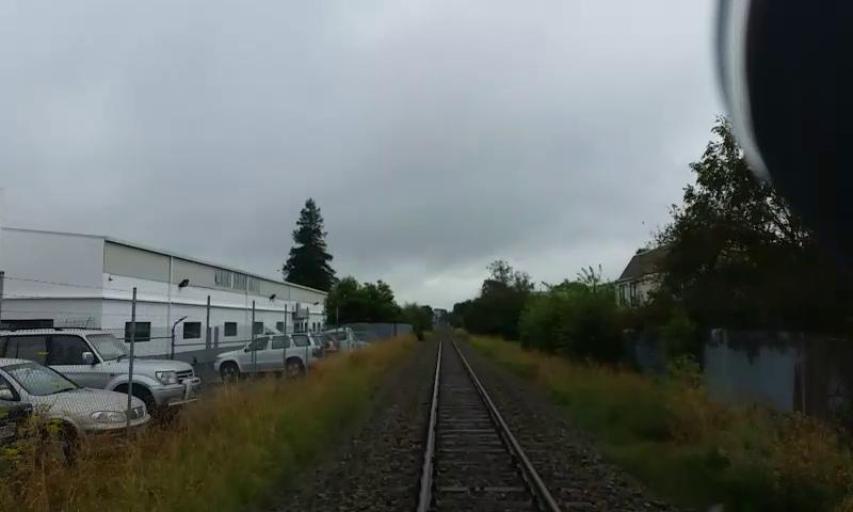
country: NZ
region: Canterbury
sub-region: Christchurch City
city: Christchurch
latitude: -43.5322
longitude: 172.6091
